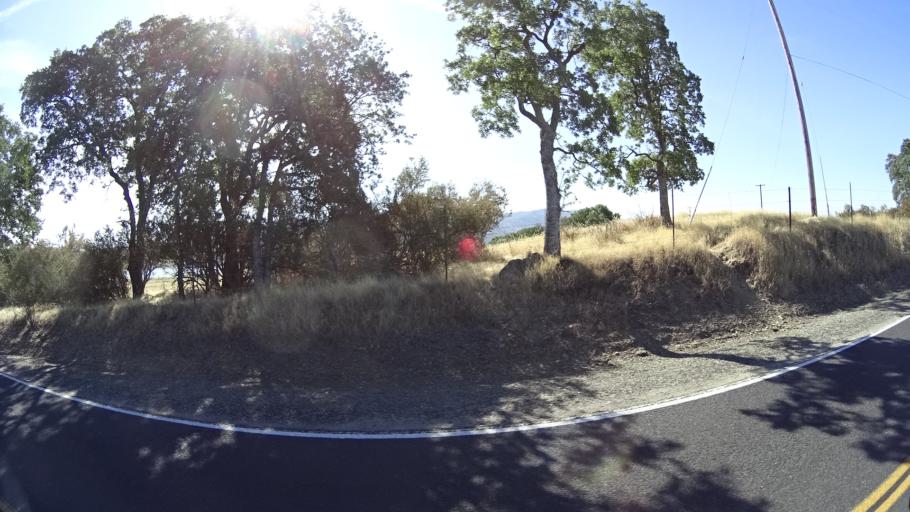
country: US
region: California
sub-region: Calaveras County
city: Valley Springs
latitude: 38.1682
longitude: -120.8134
